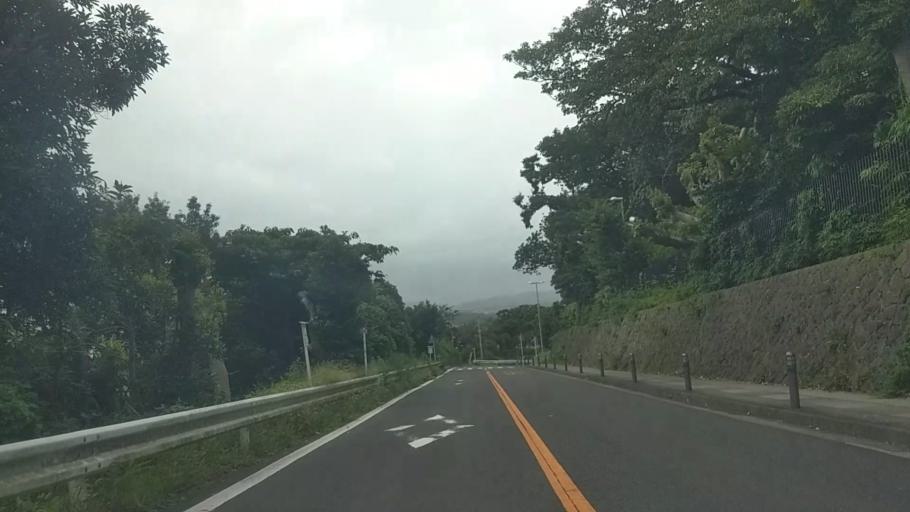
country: JP
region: Kanagawa
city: Yokosuka
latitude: 35.2553
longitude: 139.7203
